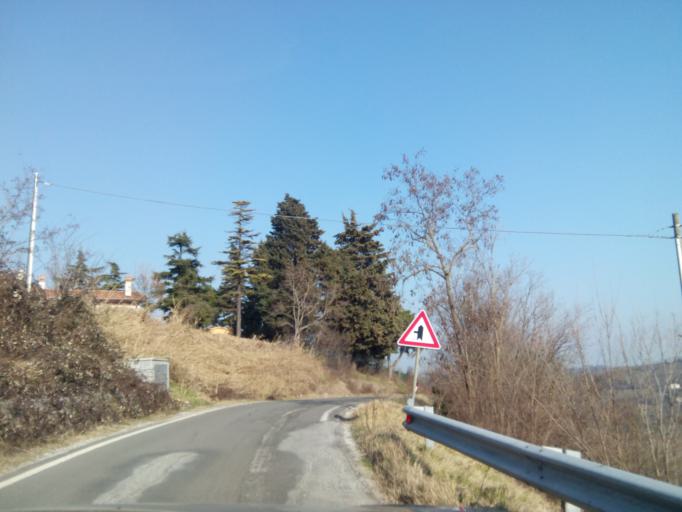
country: IT
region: Emilia-Romagna
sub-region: Provincia di Ravenna
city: Riolo Terme
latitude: 44.3093
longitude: 11.6866
